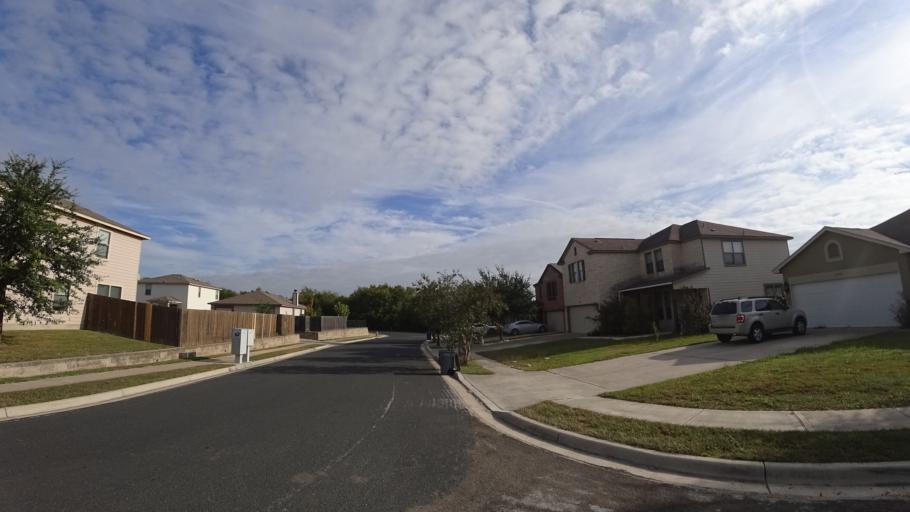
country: US
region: Texas
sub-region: Travis County
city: Austin
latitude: 30.1982
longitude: -97.7274
